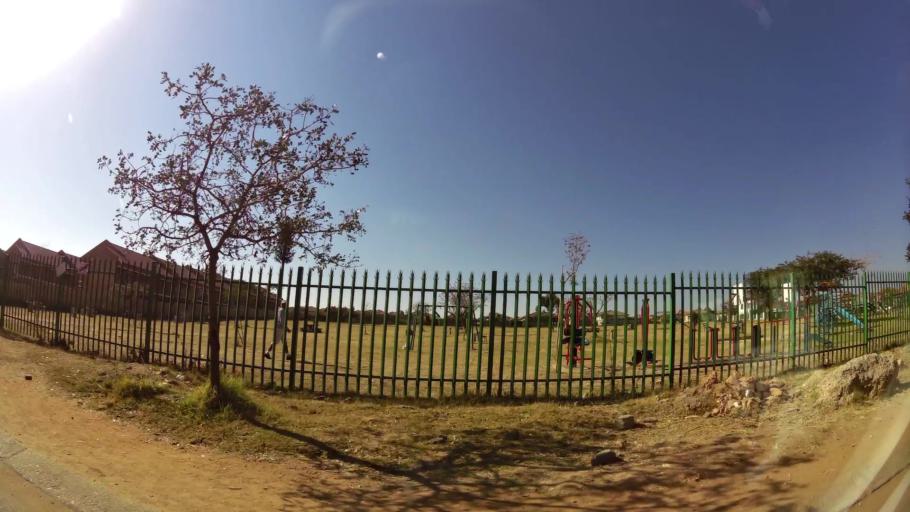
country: ZA
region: Gauteng
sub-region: Ekurhuleni Metropolitan Municipality
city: Tembisa
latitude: -26.0429
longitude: 28.1981
